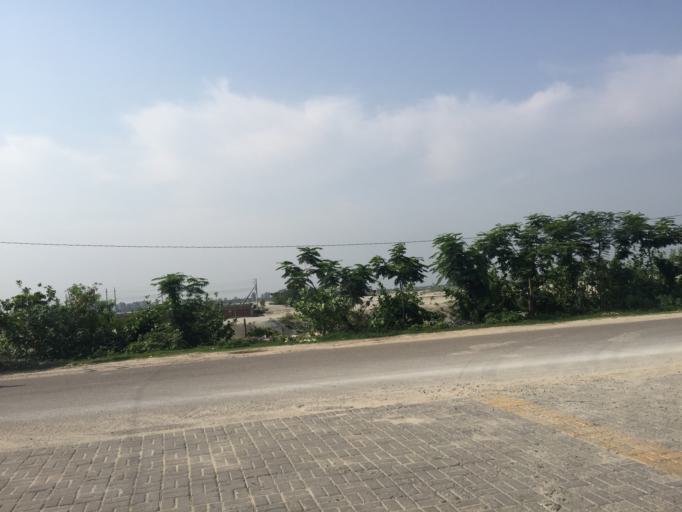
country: BD
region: Dhaka
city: Paltan
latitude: 23.8002
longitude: 90.4487
